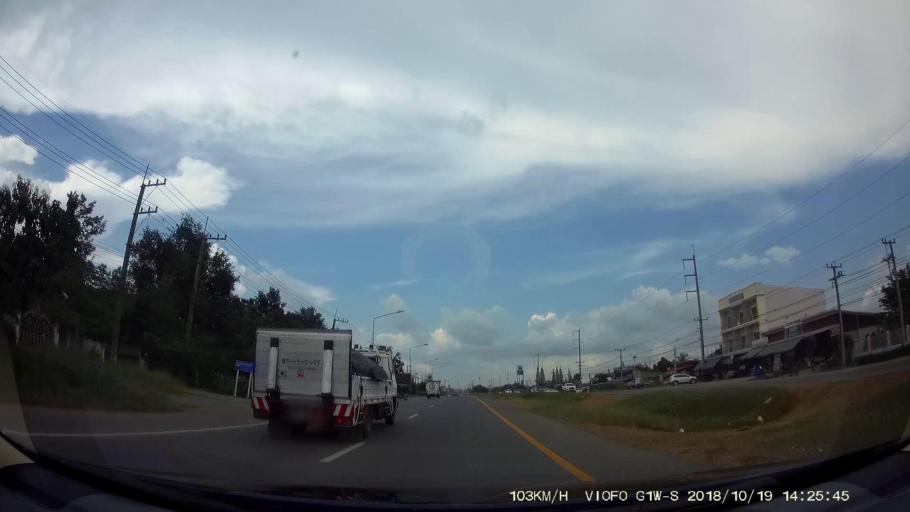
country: TH
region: Chaiyaphum
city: Kaeng Khro
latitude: 16.0981
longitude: 102.2628
